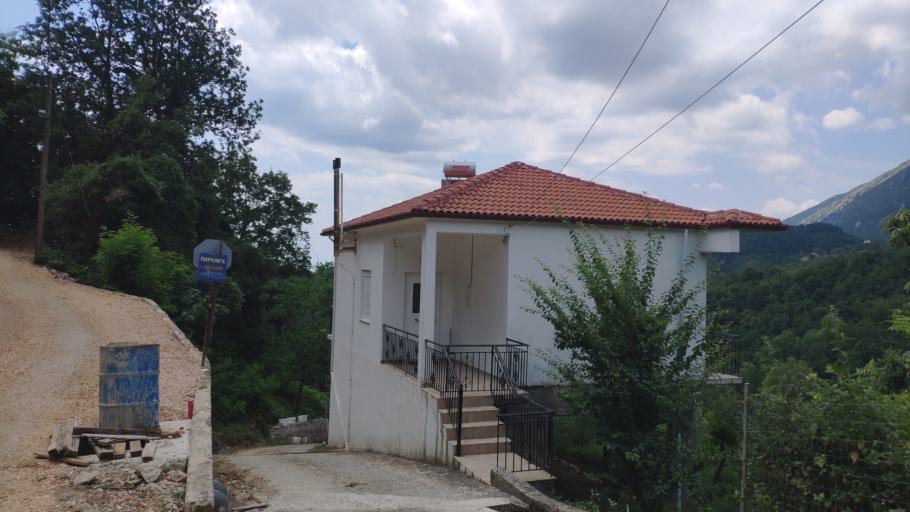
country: GR
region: Epirus
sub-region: Nomos Artas
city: Agios Dimitrios
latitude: 39.3219
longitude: 20.9976
